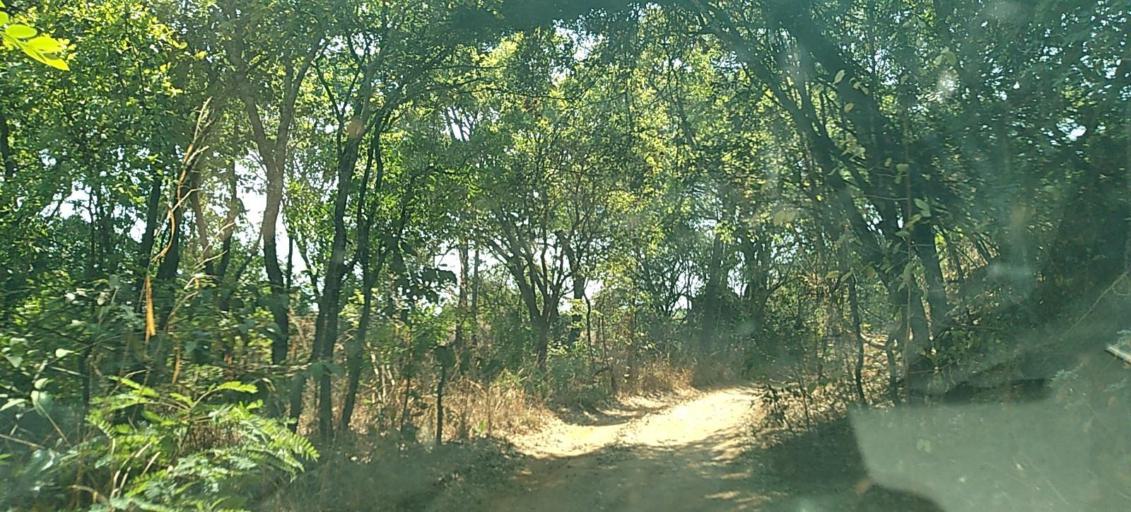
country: ZM
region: North-Western
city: Solwezi
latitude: -12.0999
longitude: 26.2835
